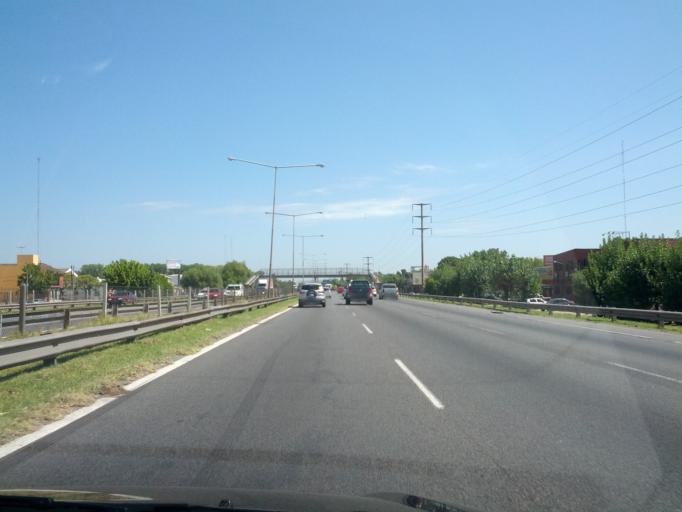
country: AR
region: Buenos Aires
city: Santa Catalina - Dique Lujan
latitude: -34.3906
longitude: -58.7435
